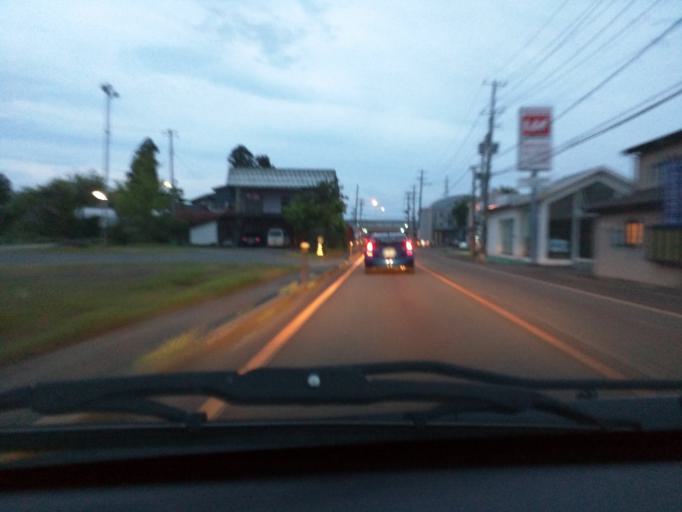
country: JP
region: Niigata
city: Kashiwazaki
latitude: 37.3582
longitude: 138.5944
